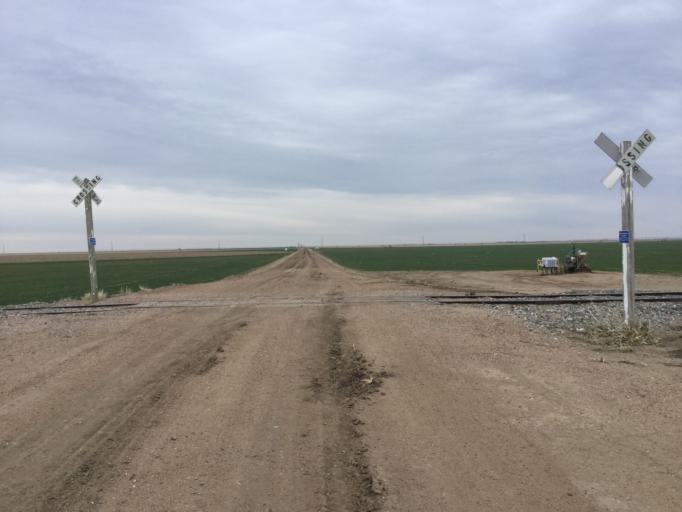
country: US
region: Kansas
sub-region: Stanton County
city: Johnson
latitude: 37.5627
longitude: -101.6715
